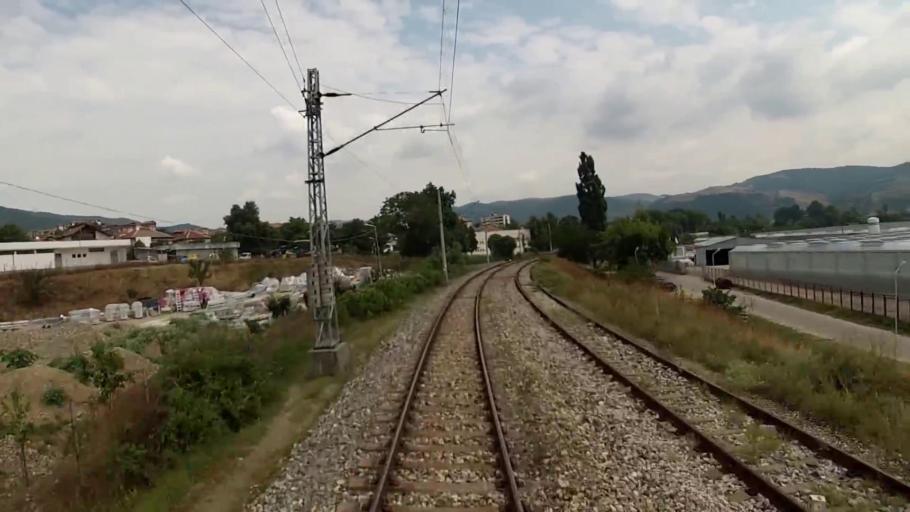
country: BG
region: Blagoevgrad
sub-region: Obshtina Simitli
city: Simitli
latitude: 41.8890
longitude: 23.1075
